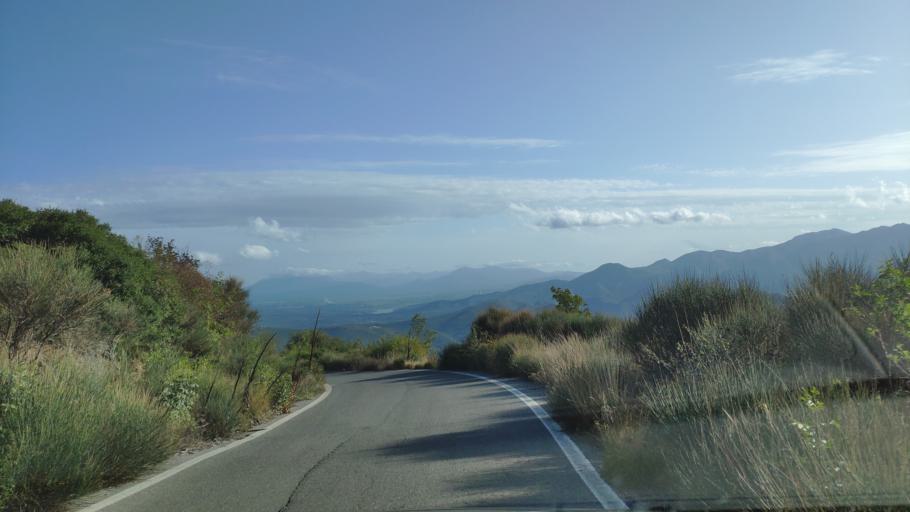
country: GR
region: Peloponnese
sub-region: Nomos Arkadias
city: Dimitsana
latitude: 37.5627
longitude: 22.0306
